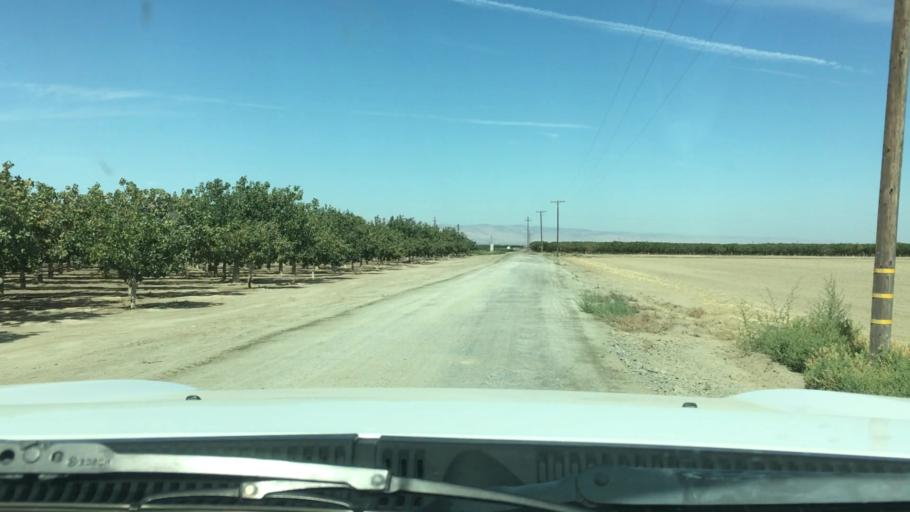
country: US
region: California
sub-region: Kern County
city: Buttonwillow
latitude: 35.3767
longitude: -119.4011
